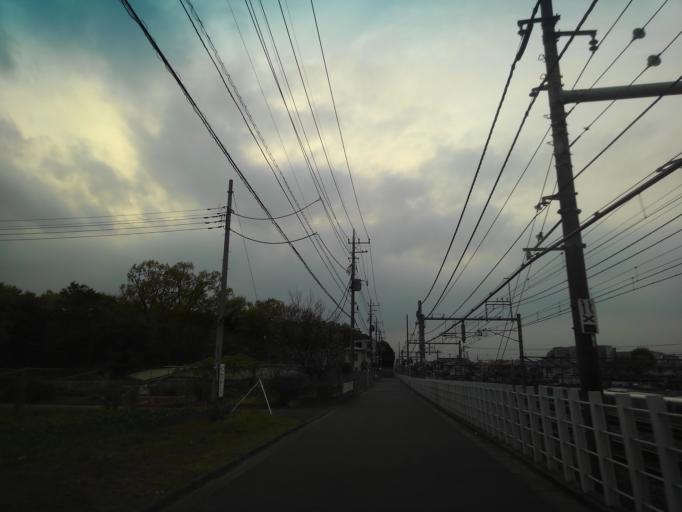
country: JP
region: Saitama
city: Tokorozawa
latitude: 35.8058
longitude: 139.4267
